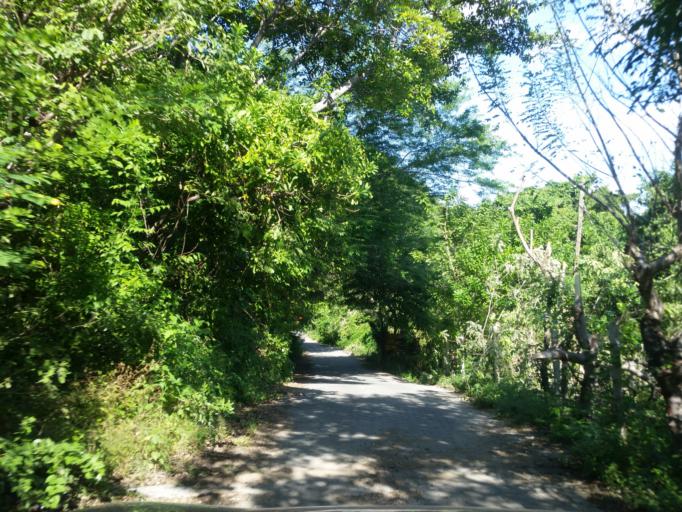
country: NI
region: Masaya
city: Catarina
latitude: 11.9412
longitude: -86.0475
